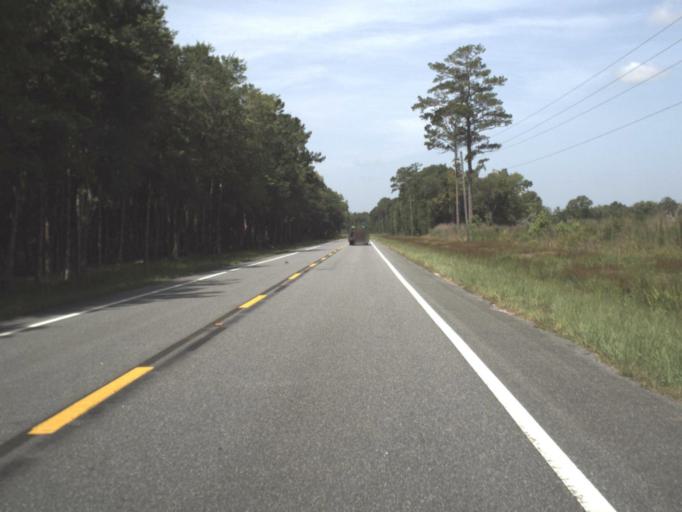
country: US
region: Florida
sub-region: Lafayette County
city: Mayo
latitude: 29.9608
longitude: -83.2379
